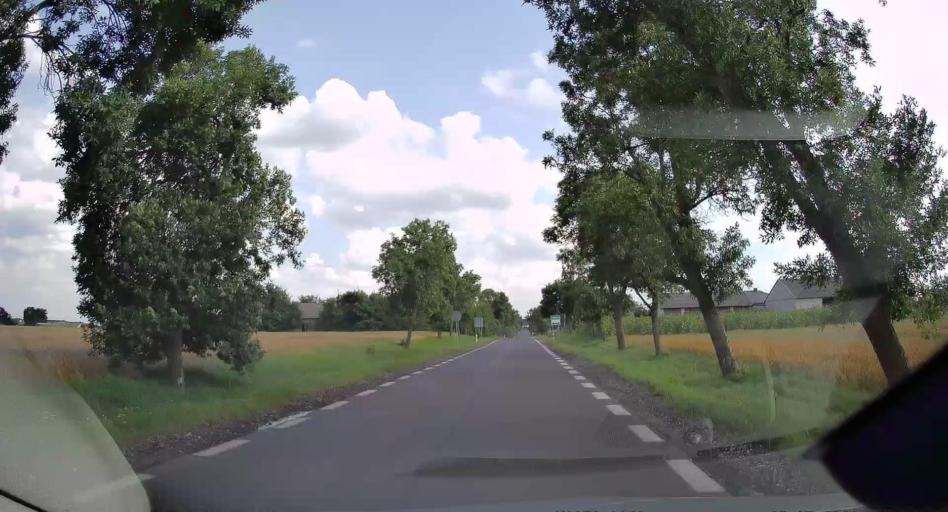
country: PL
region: Lodz Voivodeship
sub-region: Powiat tomaszowski
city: Rzeczyca
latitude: 51.6323
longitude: 20.2907
